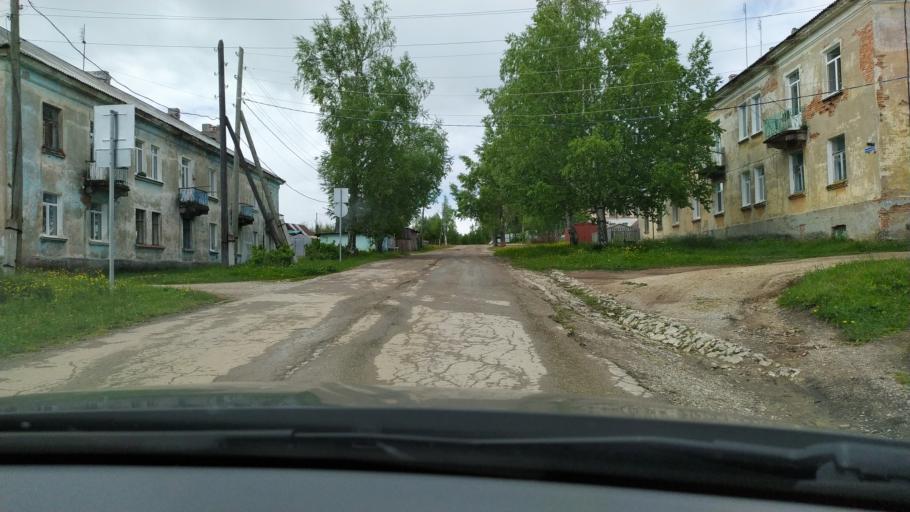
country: RU
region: Perm
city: Gremyachinsk
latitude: 58.5108
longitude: 57.8306
